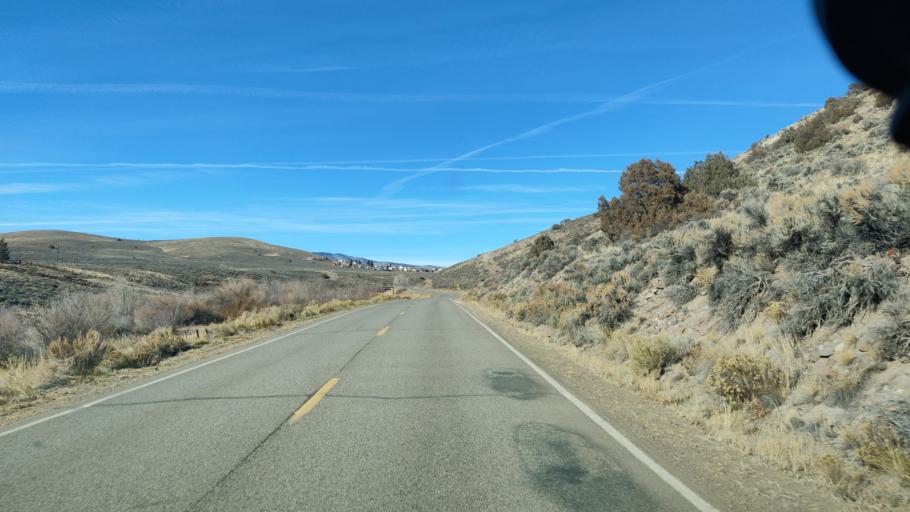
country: US
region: Colorado
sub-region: Gunnison County
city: Gunnison
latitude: 38.5658
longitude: -106.9579
